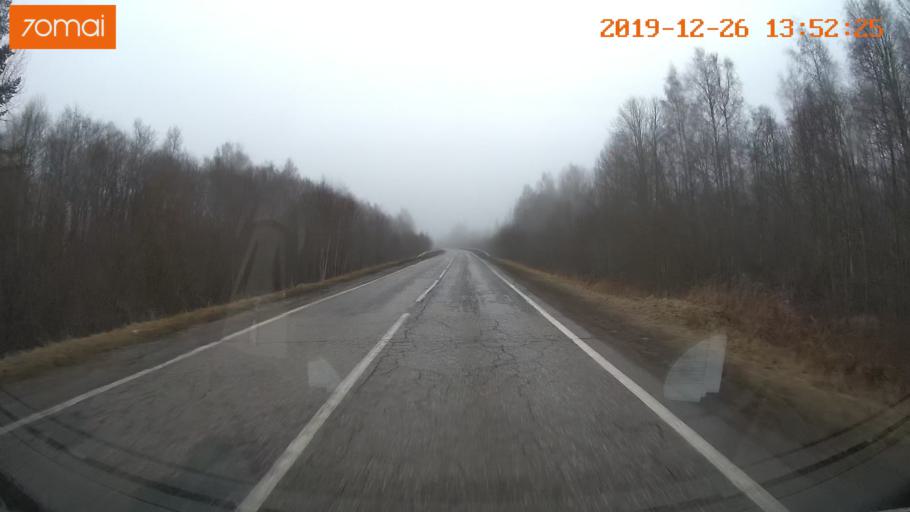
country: RU
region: Jaroslavl
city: Poshekhon'ye
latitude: 58.6321
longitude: 38.6014
